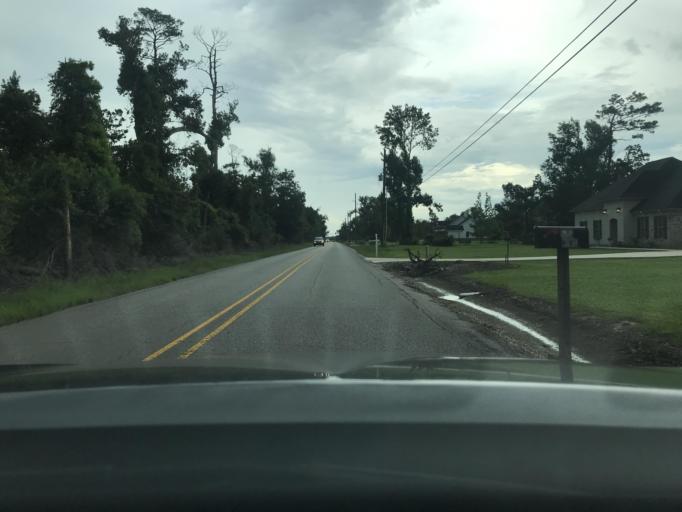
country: US
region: Louisiana
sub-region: Calcasieu Parish
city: Westlake
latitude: 30.2570
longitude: -93.2369
